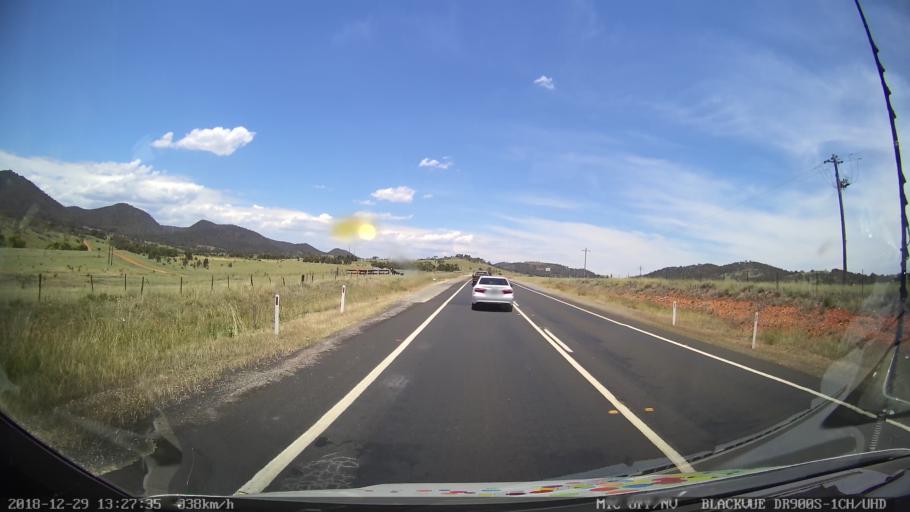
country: AU
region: New South Wales
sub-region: Cooma-Monaro
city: Cooma
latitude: -35.8669
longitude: 149.1599
